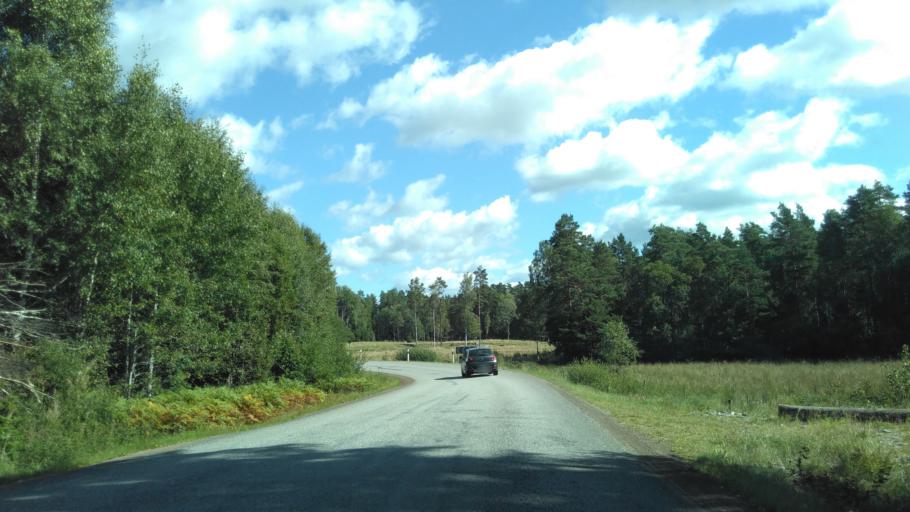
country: SE
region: Vaestra Goetaland
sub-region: Herrljunga Kommun
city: Herrljunga
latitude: 58.0957
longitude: 13.0528
